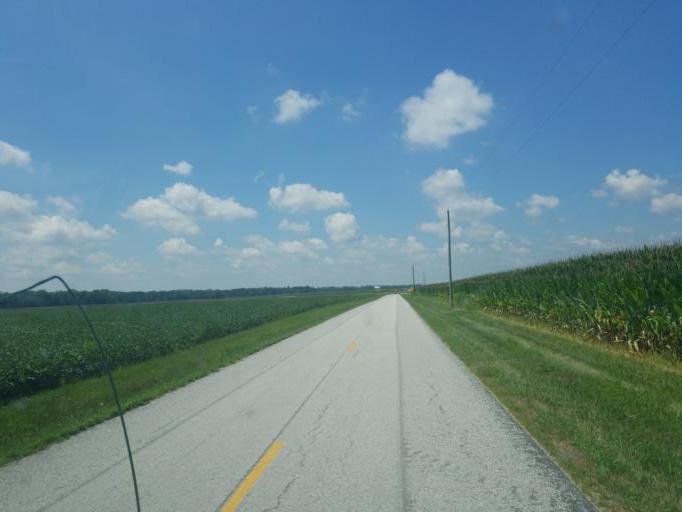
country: US
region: Ohio
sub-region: Allen County
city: Spencerville
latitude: 40.6666
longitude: -84.4319
